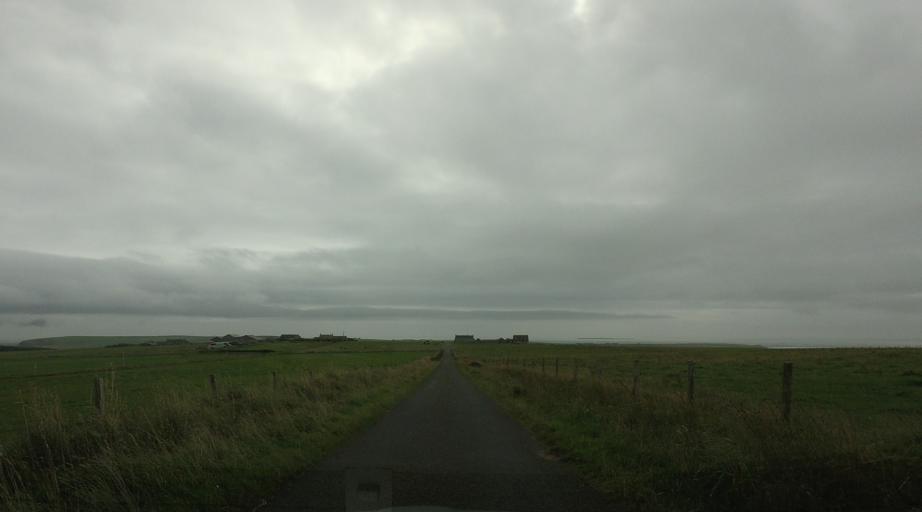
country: GB
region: Scotland
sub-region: Orkney Islands
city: Orkney
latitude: 58.7664
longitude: -2.9638
